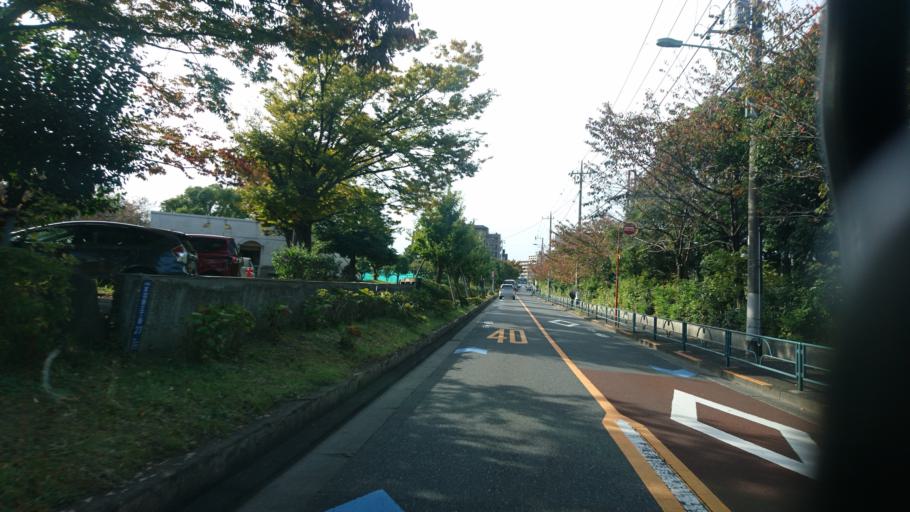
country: JP
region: Kanagawa
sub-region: Kawasaki-shi
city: Kawasaki
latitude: 35.5461
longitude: 139.7389
